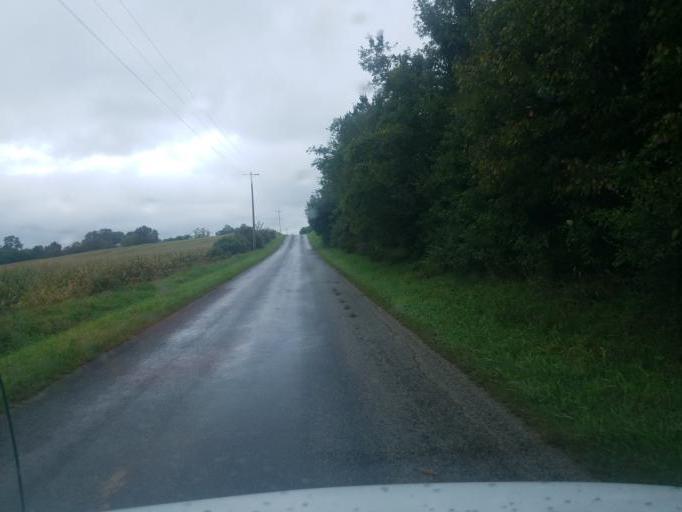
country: US
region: Ohio
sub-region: Ashland County
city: Ashland
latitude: 40.8279
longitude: -82.1974
